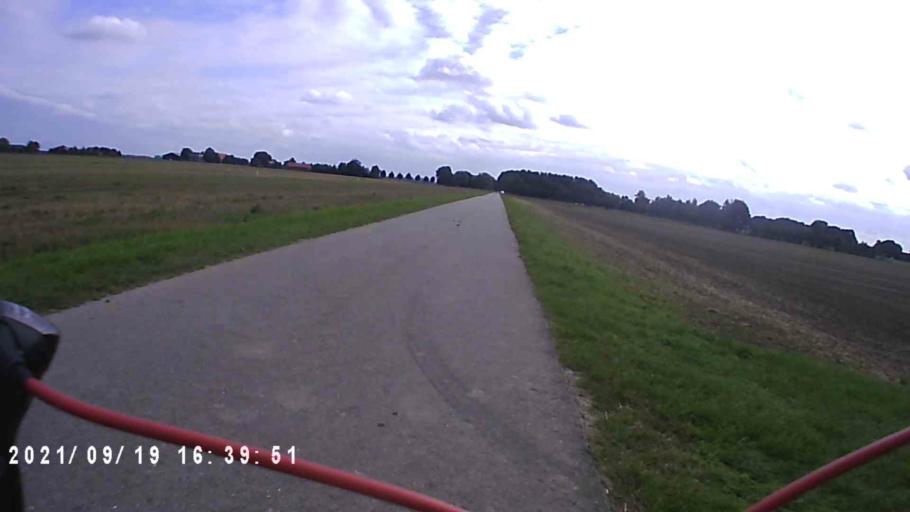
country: NL
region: Groningen
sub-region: Gemeente  Oldambt
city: Winschoten
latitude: 53.1880
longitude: 7.1323
